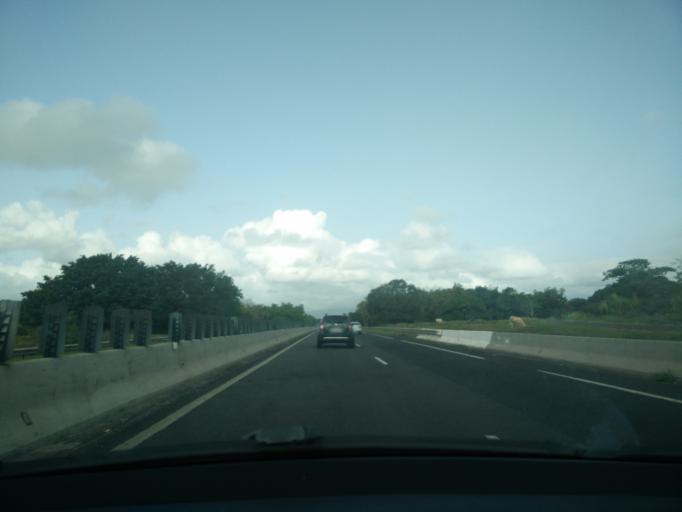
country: GP
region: Guadeloupe
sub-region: Guadeloupe
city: Baie-Mahault
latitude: 16.2679
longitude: -61.5581
